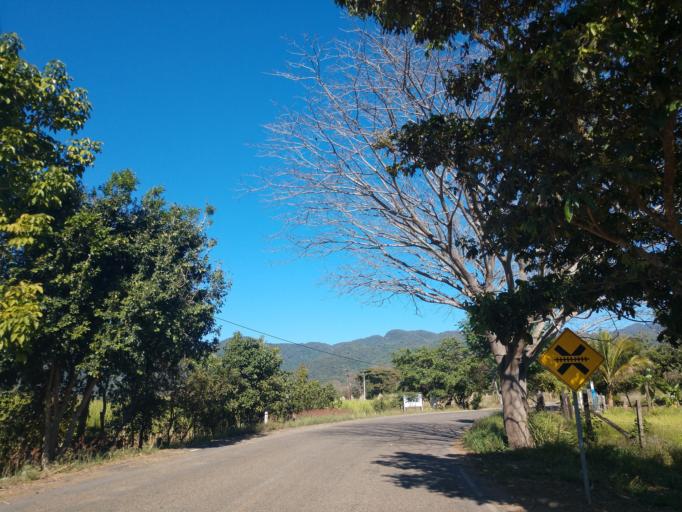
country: MX
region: Nayarit
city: Compostela
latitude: 21.2724
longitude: -104.8861
